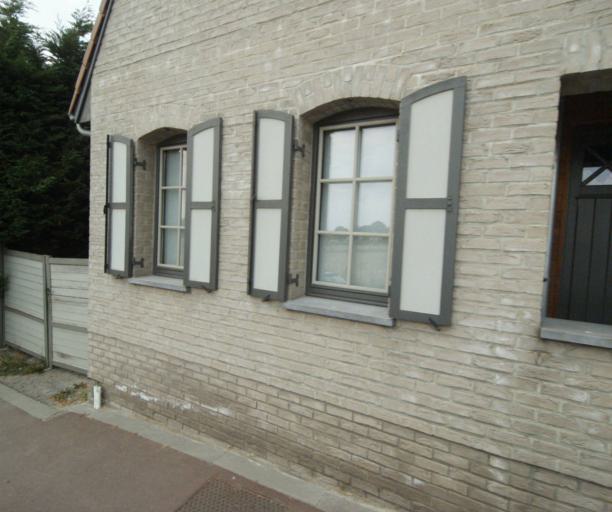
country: FR
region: Nord-Pas-de-Calais
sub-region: Departement du Nord
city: Neuville-en-Ferrain
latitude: 50.7461
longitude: 3.1507
